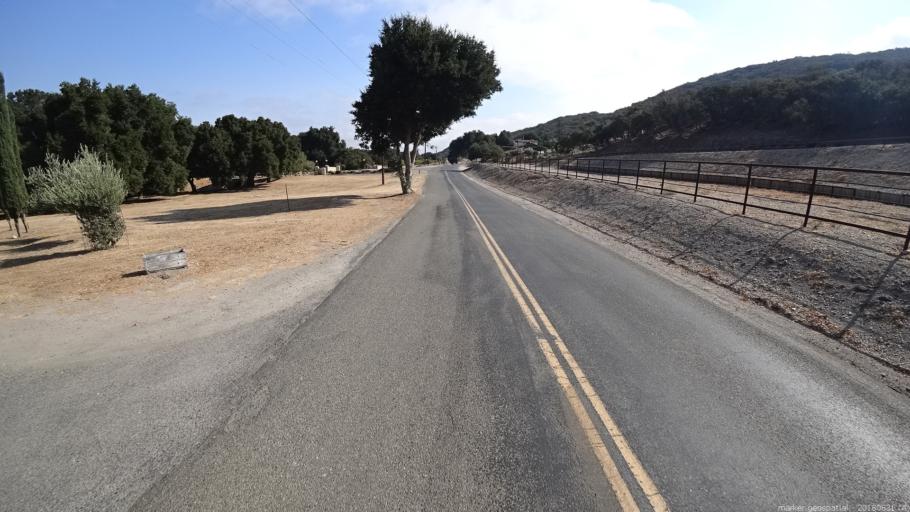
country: US
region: California
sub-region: Monterey County
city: King City
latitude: 36.1571
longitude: -121.1679
